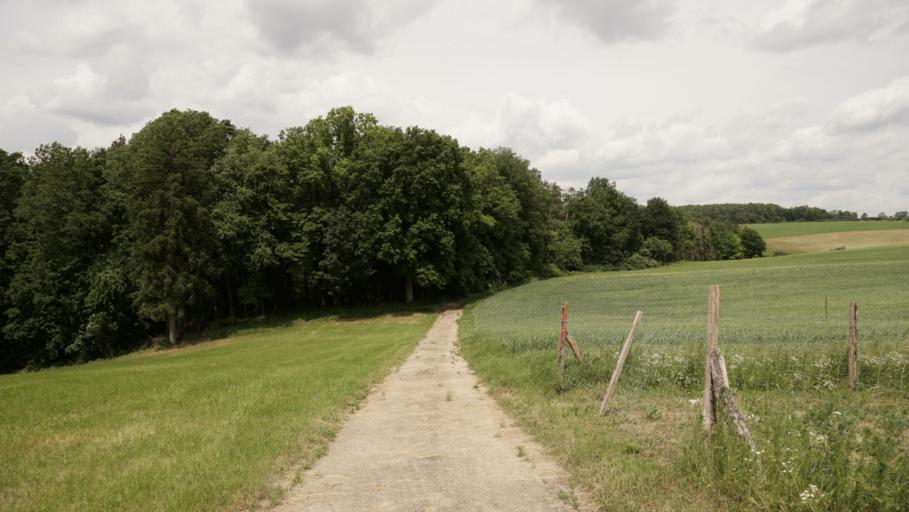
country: DE
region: Baden-Wuerttemberg
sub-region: Karlsruhe Region
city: Billigheim
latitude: 49.3788
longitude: 9.2128
